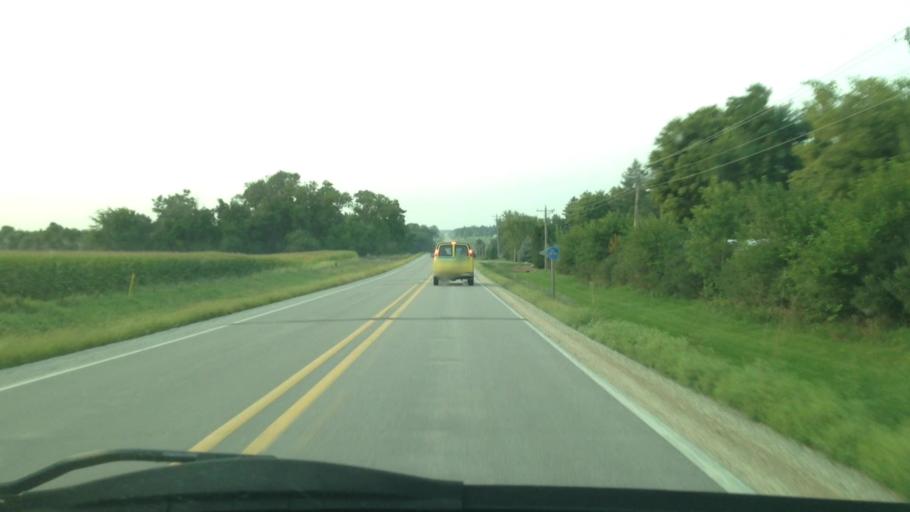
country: US
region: Iowa
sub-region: Benton County
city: Atkins
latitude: 42.0518
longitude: -91.8692
